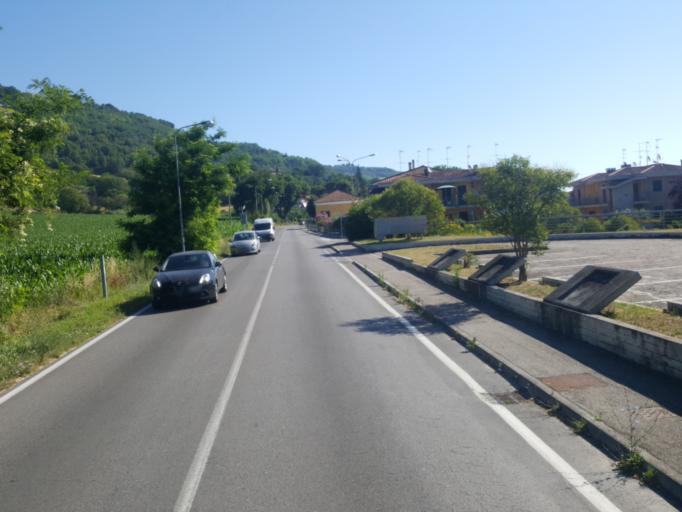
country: IT
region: The Marches
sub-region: Provincia di Pesaro e Urbino
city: Rio Salso-Case Bernardi
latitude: 43.8330
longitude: 12.6856
